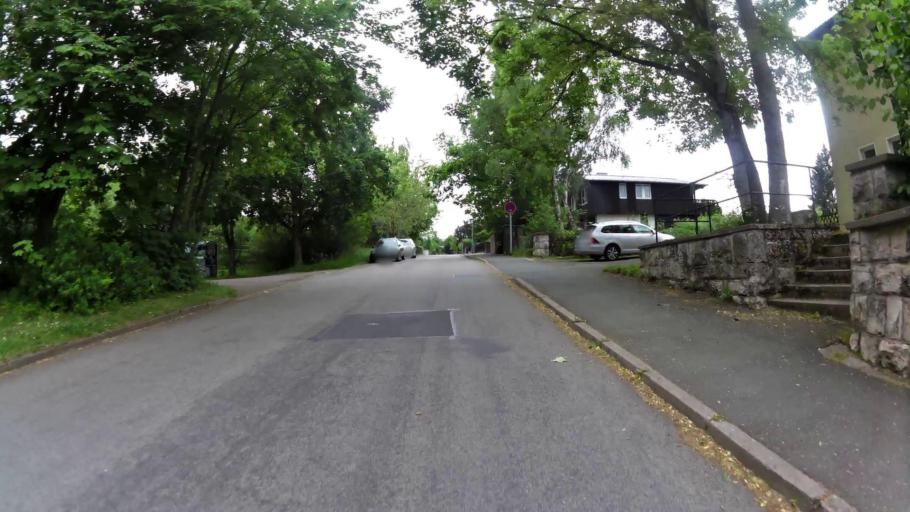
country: DE
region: Thuringia
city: Weimar
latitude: 50.9751
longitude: 11.3086
